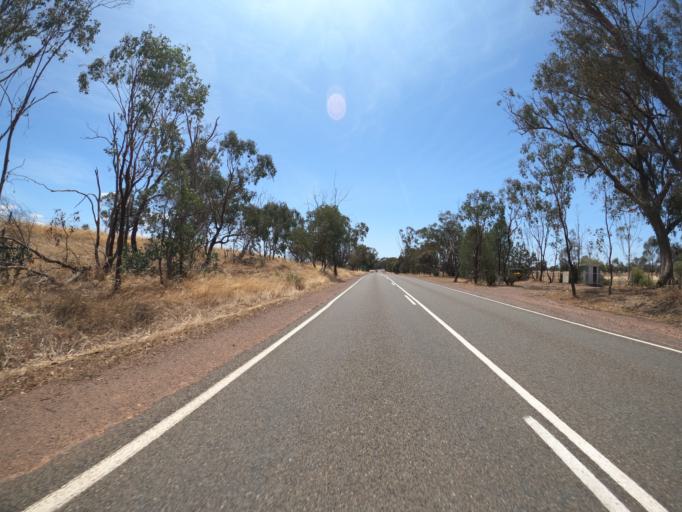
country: AU
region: Victoria
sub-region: Benalla
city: Benalla
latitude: -36.3221
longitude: 145.9586
